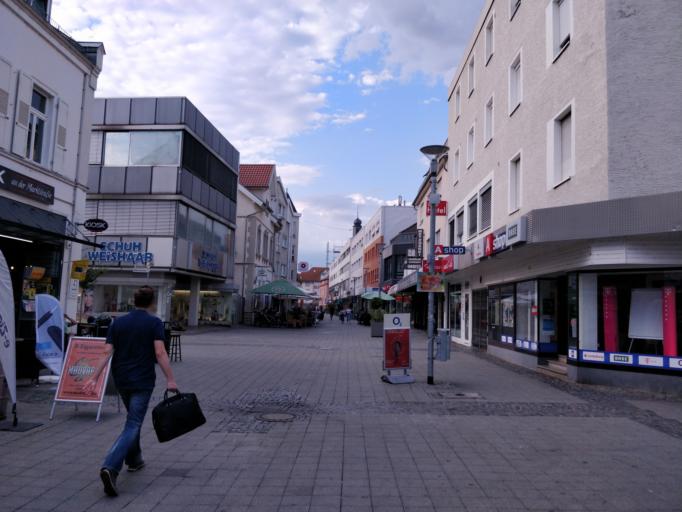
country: DE
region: Hesse
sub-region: Regierungsbezirk Darmstadt
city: Russelsheim
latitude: 49.9932
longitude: 8.4123
